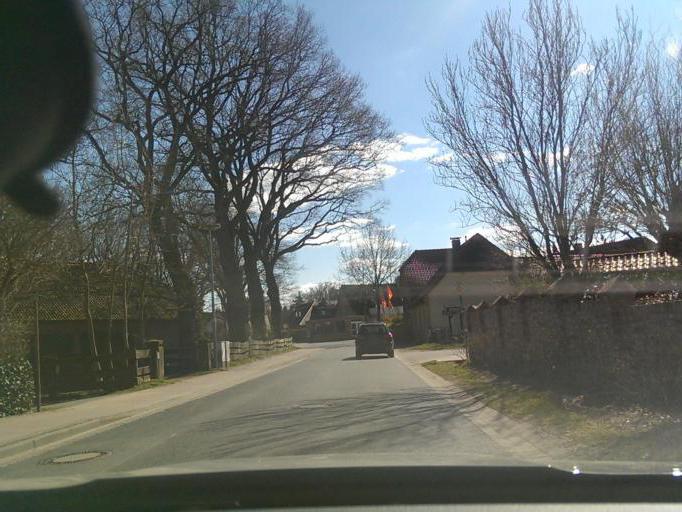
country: DE
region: Lower Saxony
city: Elze
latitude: 52.5608
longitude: 9.7339
